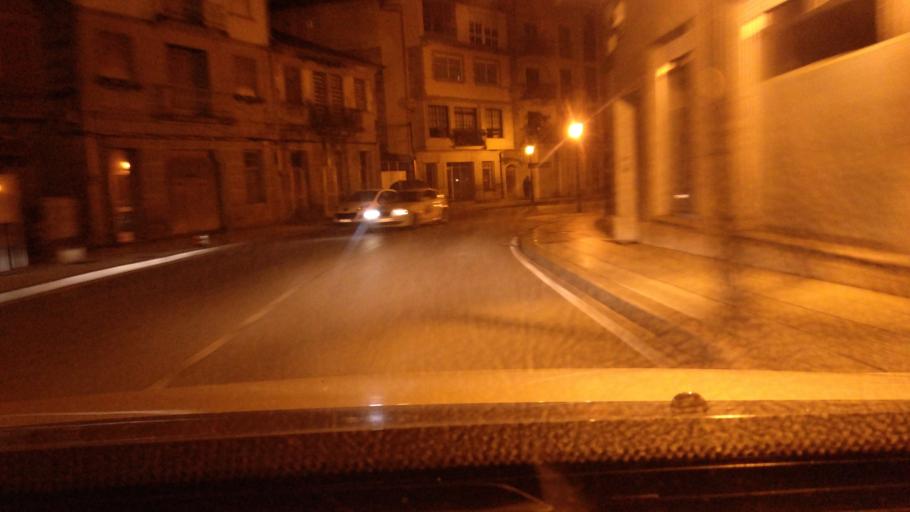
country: ES
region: Galicia
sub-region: Provincia de Pontevedra
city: Moana
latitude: 42.2797
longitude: -8.7376
